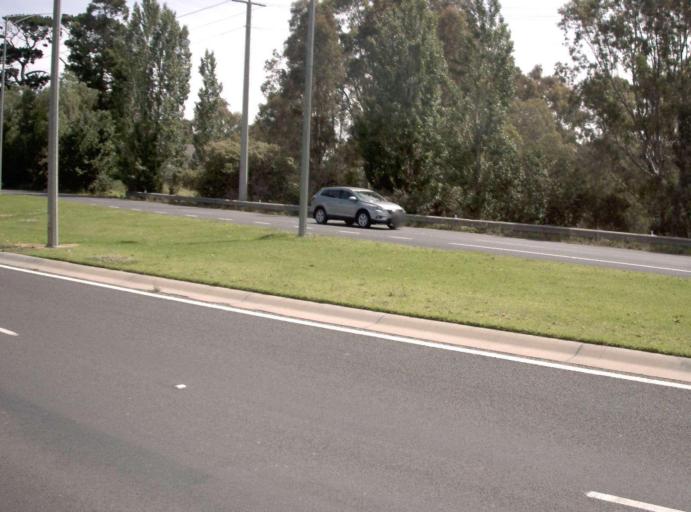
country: AU
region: Victoria
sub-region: Wellington
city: Heyfield
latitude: -38.1493
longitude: 146.7902
